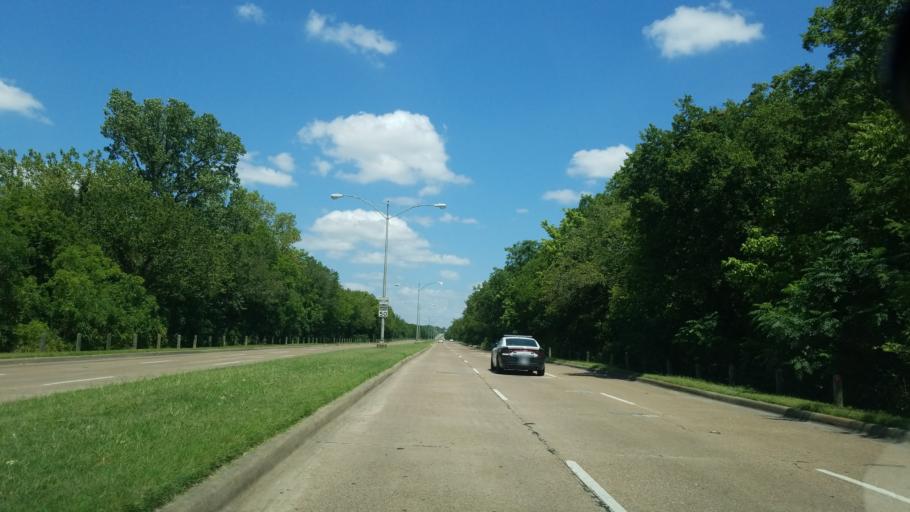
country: US
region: Texas
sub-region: Dallas County
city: Dallas
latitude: 32.7493
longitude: -96.7232
